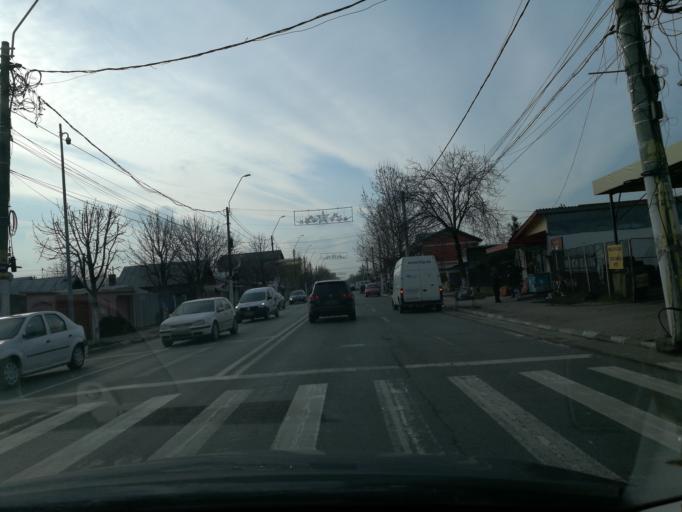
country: RO
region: Ilfov
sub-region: Voluntari City
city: Voluntari
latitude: 44.4933
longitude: 26.1728
